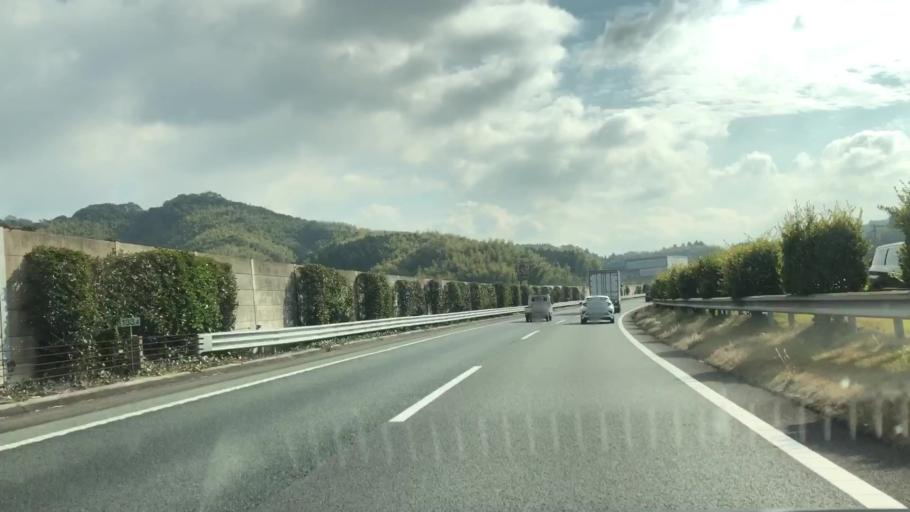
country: JP
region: Fukuoka
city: Setakamachi-takayanagi
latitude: 33.0860
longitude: 130.5411
